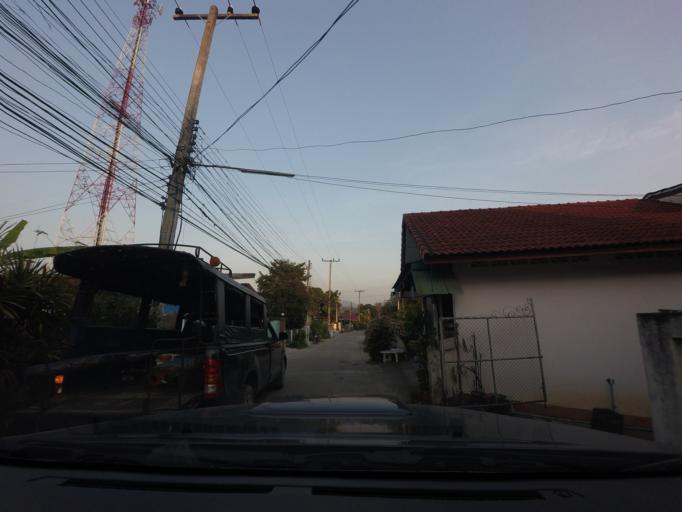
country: TH
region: Chiang Mai
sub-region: Amphoe Chiang Dao
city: Chiang Dao
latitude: 19.3675
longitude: 98.9626
